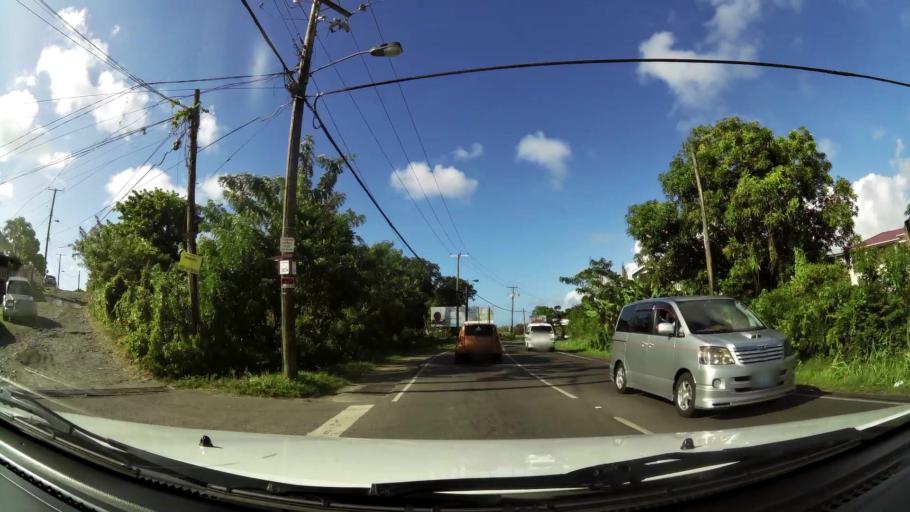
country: LC
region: Castries Quarter
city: Bisee
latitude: 14.0456
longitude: -60.9698
